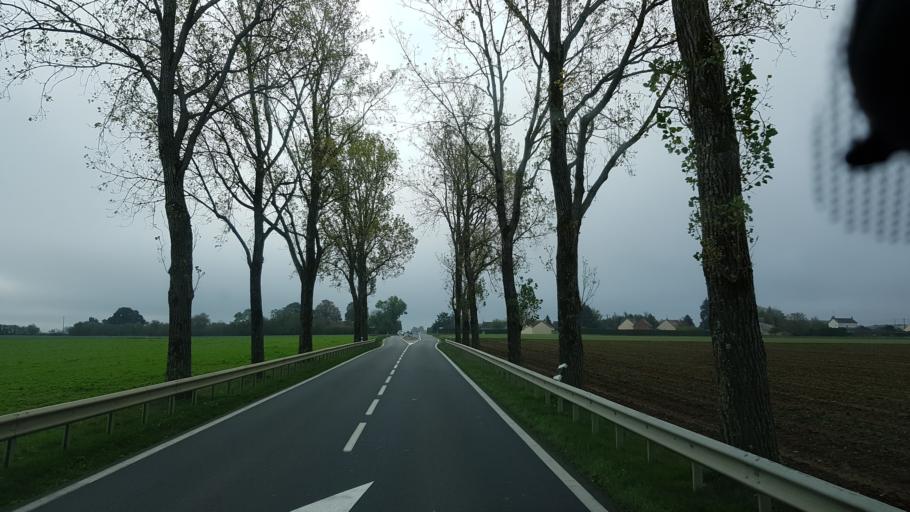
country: FR
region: Ile-de-France
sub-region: Departement de l'Essonne
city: Corbreuse
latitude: 48.4265
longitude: 1.9626
